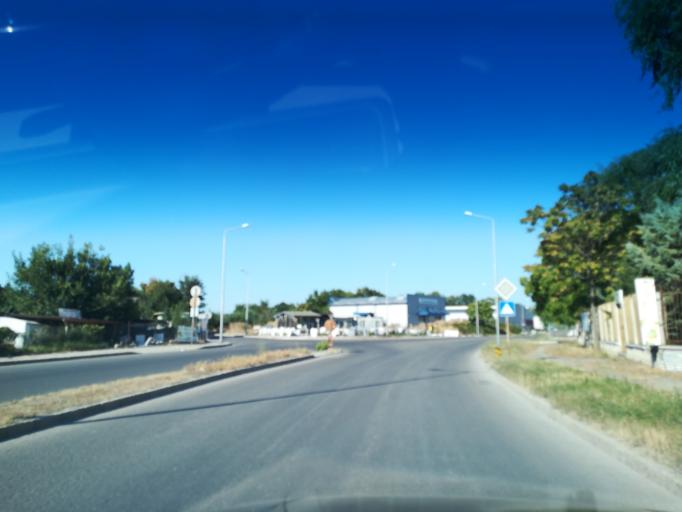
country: BG
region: Plovdiv
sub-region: Obshtina Plovdiv
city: Plovdiv
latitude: 42.1650
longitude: 24.7747
